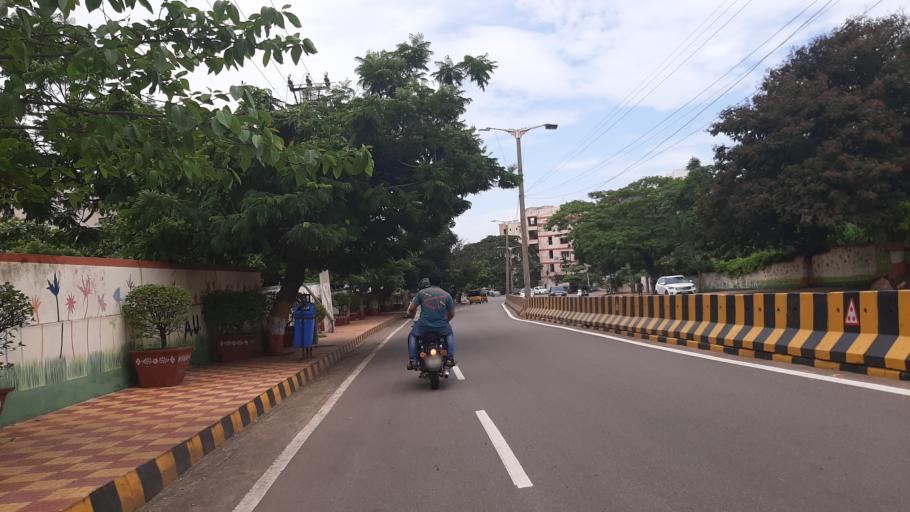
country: IN
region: Andhra Pradesh
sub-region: Vishakhapatnam
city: Yarada
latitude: 17.7225
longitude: 83.3291
